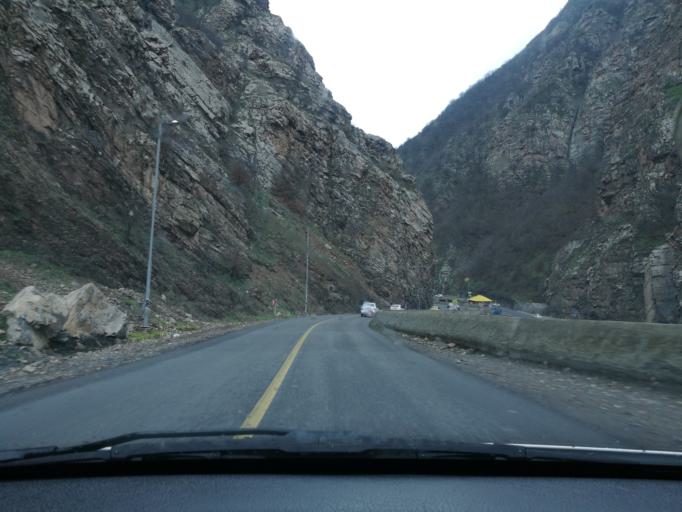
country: IR
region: Mazandaran
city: Chalus
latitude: 36.2628
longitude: 51.2651
